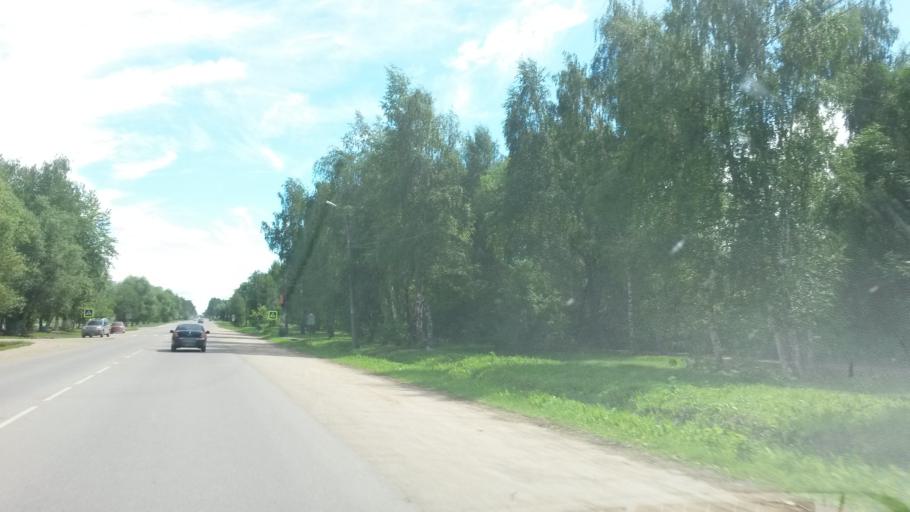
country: RU
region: Ivanovo
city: Zavolzhsk
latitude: 57.4851
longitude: 42.1442
